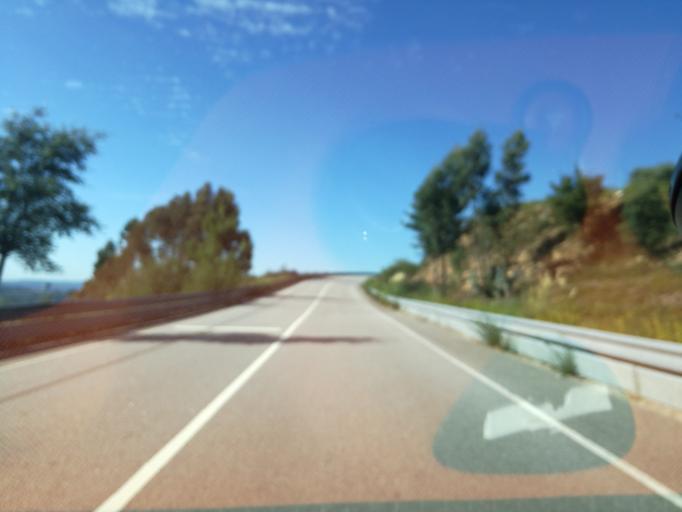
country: PT
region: Porto
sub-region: Pacos de Ferreira
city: Seroa
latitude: 41.2670
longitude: -8.4417
